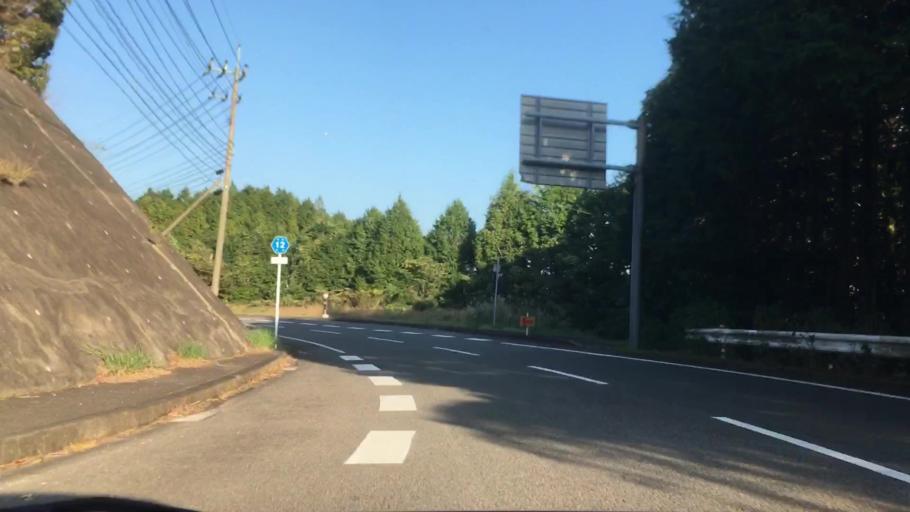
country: JP
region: Nagasaki
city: Sasebo
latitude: 32.9726
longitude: 129.6989
